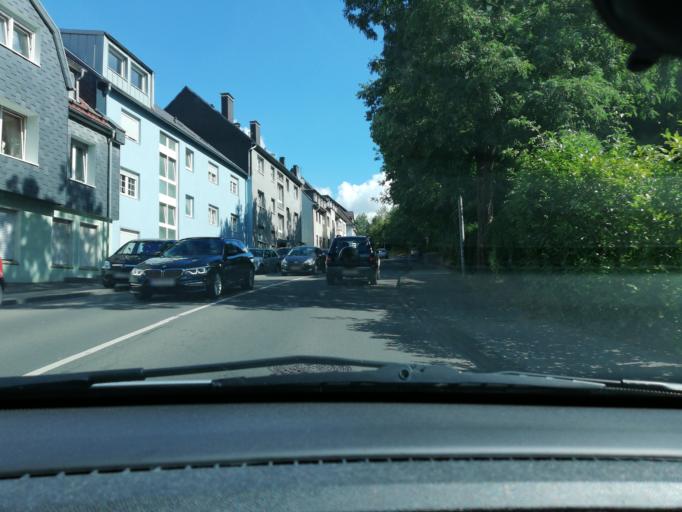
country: DE
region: North Rhine-Westphalia
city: Gevelsberg
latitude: 51.3243
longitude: 7.3372
